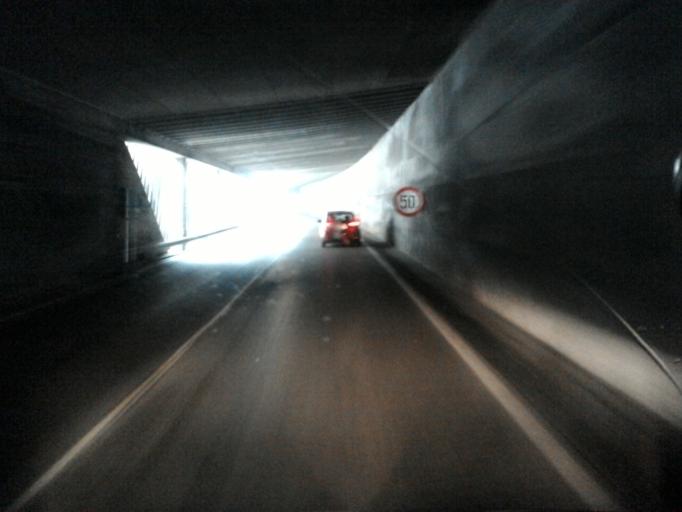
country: AT
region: Tyrol
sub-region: Politischer Bezirk Lienz
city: Matrei in Osttirol
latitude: 47.0756
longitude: 12.5316
